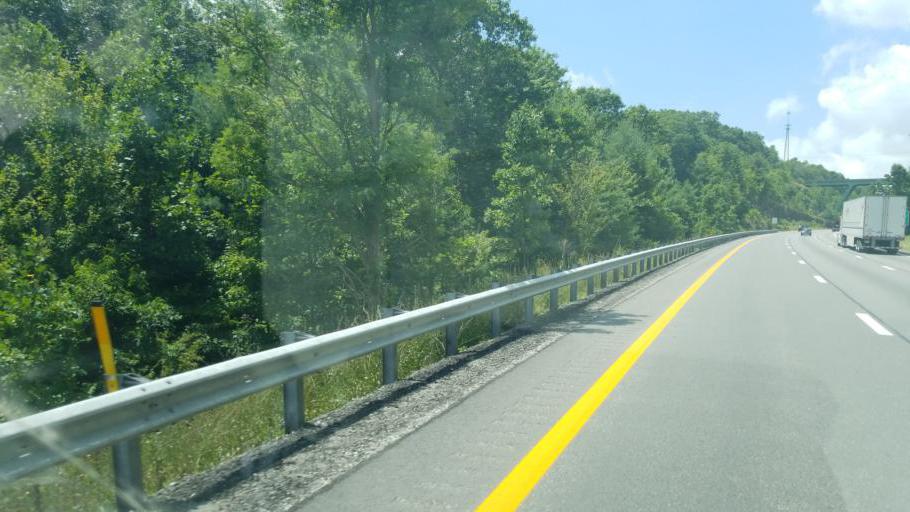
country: US
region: West Virginia
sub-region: Raleigh County
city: Beaver
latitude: 37.7224
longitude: -81.1772
